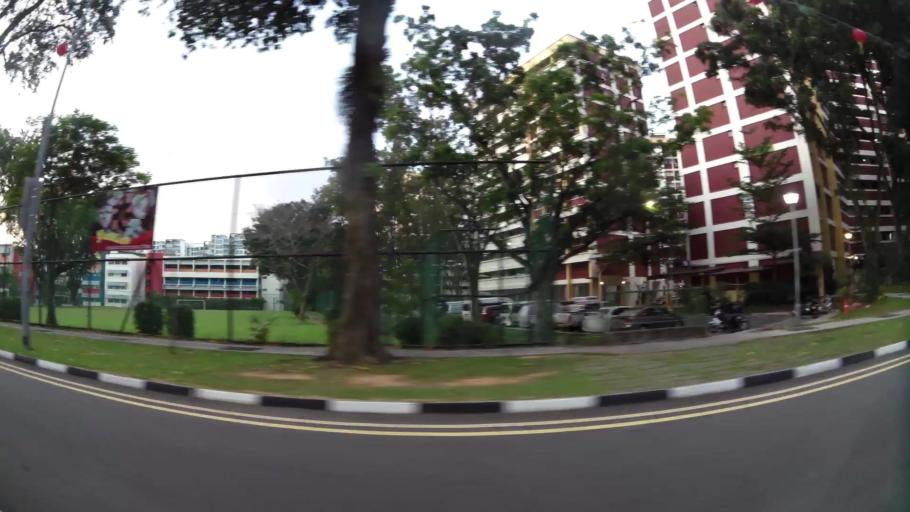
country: MY
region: Johor
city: Kampung Pasir Gudang Baru
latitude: 1.4355
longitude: 103.8313
